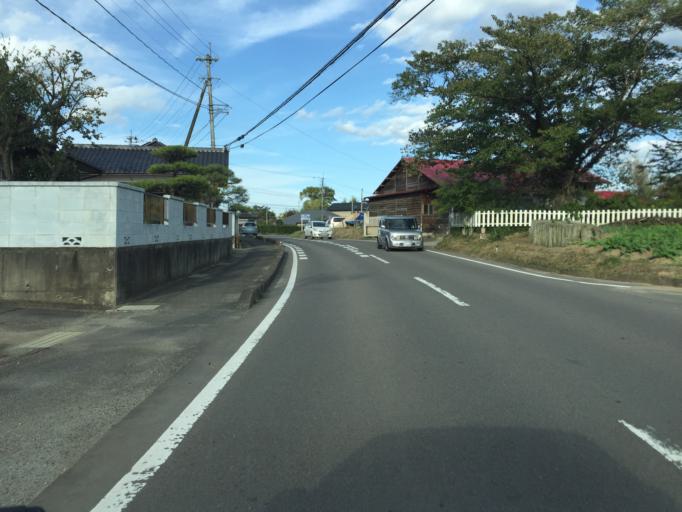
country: JP
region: Fukushima
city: Fukushima-shi
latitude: 37.7082
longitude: 140.4300
